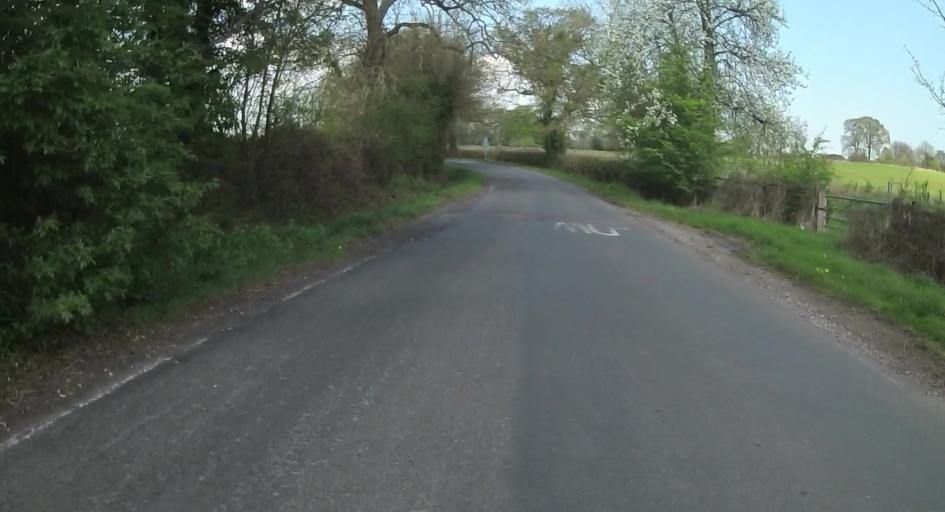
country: GB
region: England
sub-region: Hampshire
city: Tadley
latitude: 51.3215
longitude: -1.0772
